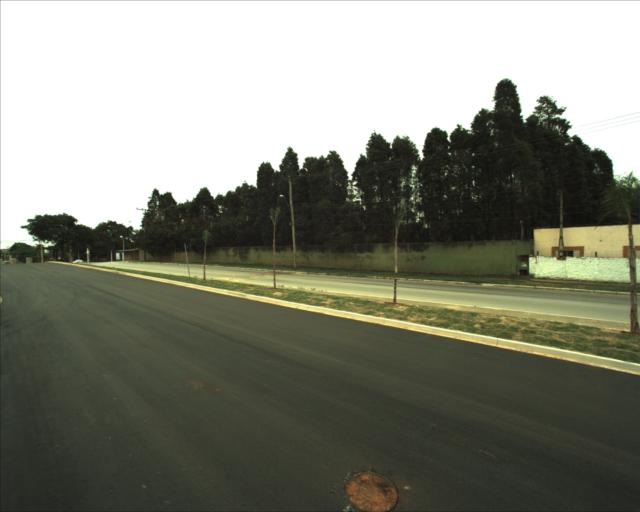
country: BR
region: Sao Paulo
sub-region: Sorocaba
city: Sorocaba
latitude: -23.4165
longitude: -47.4299
